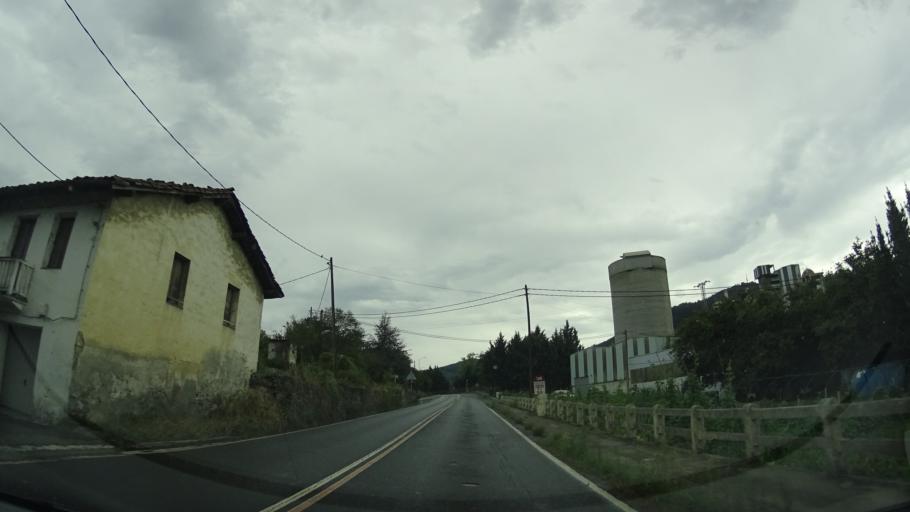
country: ES
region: Basque Country
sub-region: Bizkaia
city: Amorebieta
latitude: 43.2041
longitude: -2.7739
